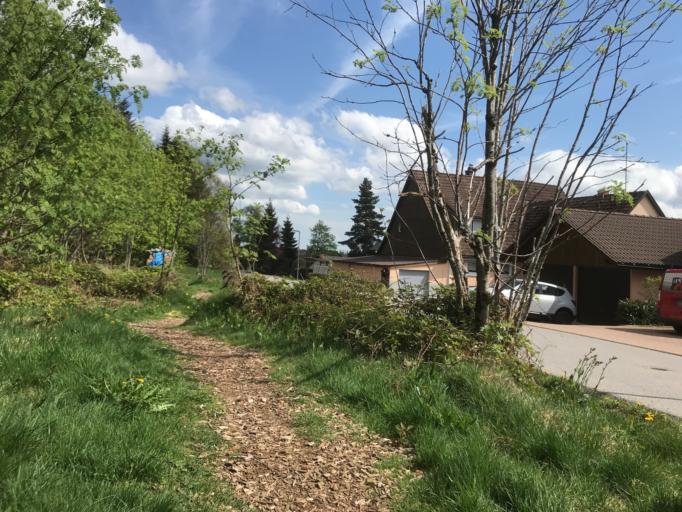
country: DE
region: Baden-Wuerttemberg
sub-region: Karlsruhe Region
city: Baiersbronn
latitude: 48.4777
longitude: 8.3094
